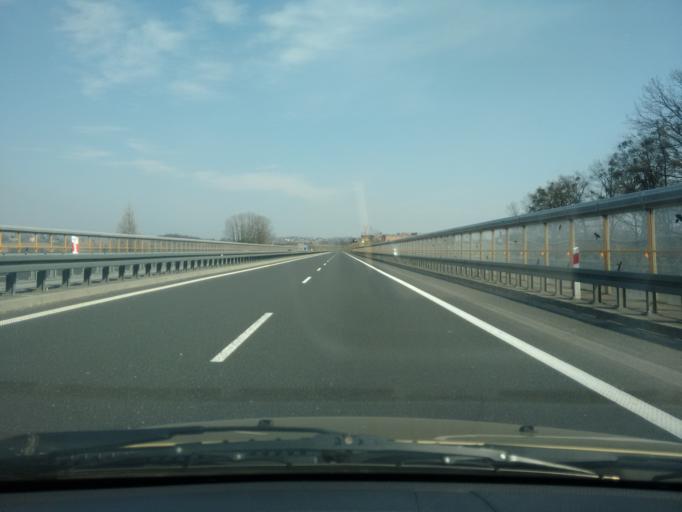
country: PL
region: Silesian Voivodeship
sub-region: Powiat cieszynski
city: Bazanowice
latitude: 49.7722
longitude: 18.7195
